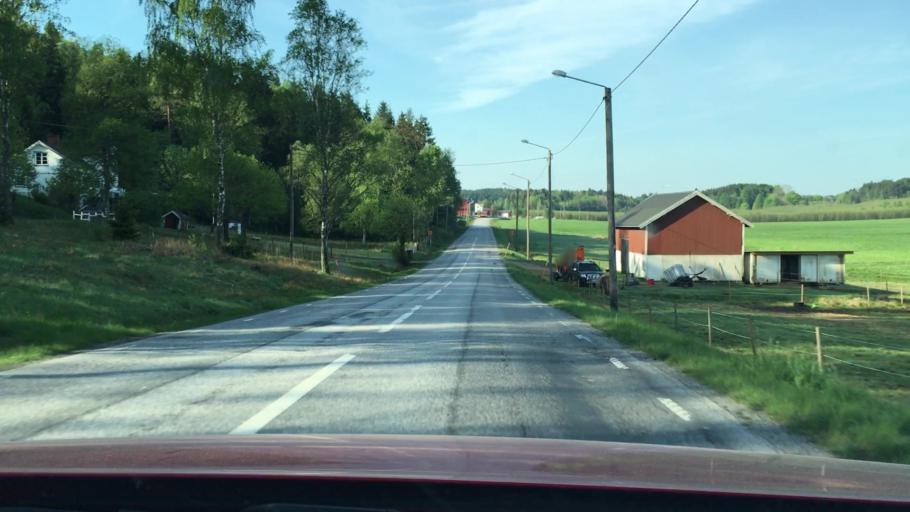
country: SE
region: Vaestra Goetaland
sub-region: Munkedals Kommun
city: Munkedal
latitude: 58.6044
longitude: 11.5587
